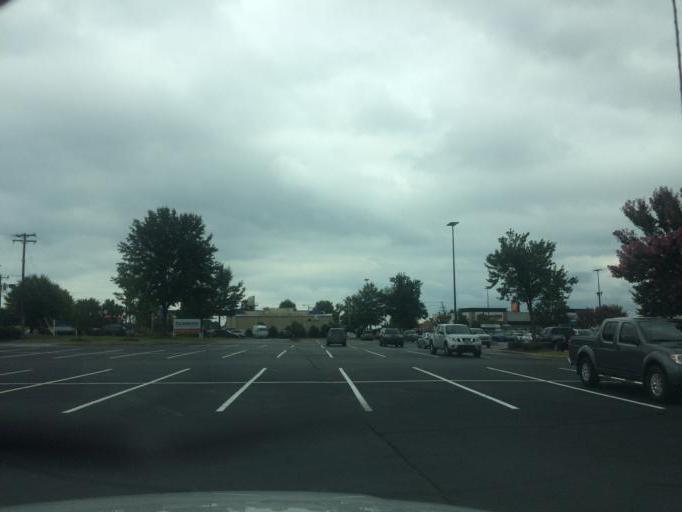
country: US
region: South Carolina
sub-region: Greenville County
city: Mauldin
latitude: 34.8294
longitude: -82.3070
